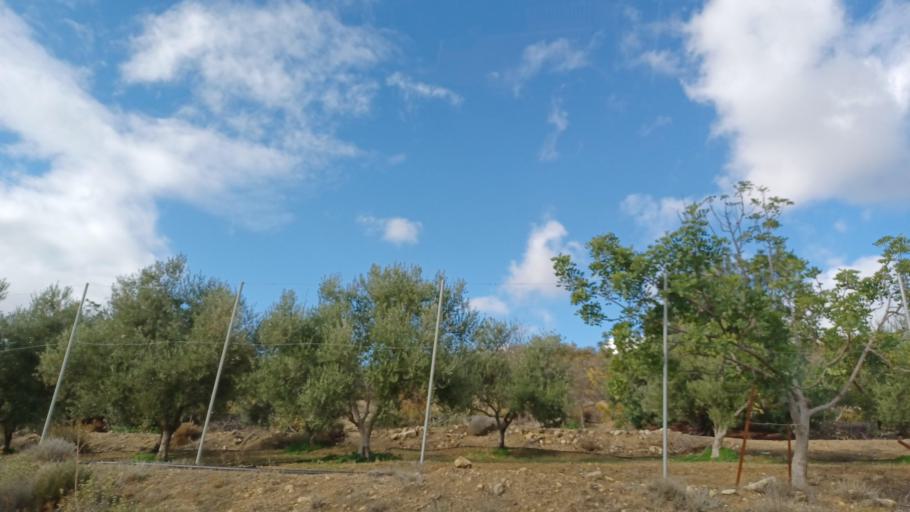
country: CY
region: Limassol
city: Sotira
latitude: 34.7466
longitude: 32.8584
